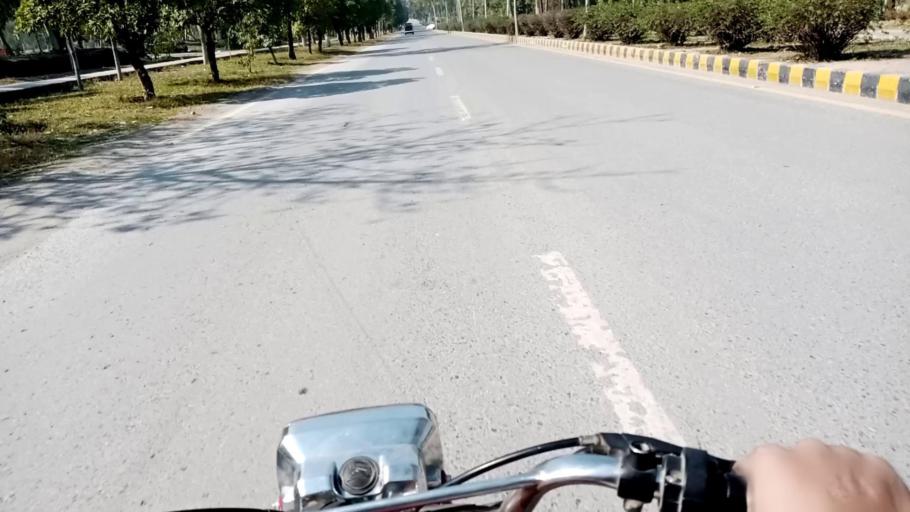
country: PK
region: Khyber Pakhtunkhwa
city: Peshawar
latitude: 33.9564
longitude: 71.4313
